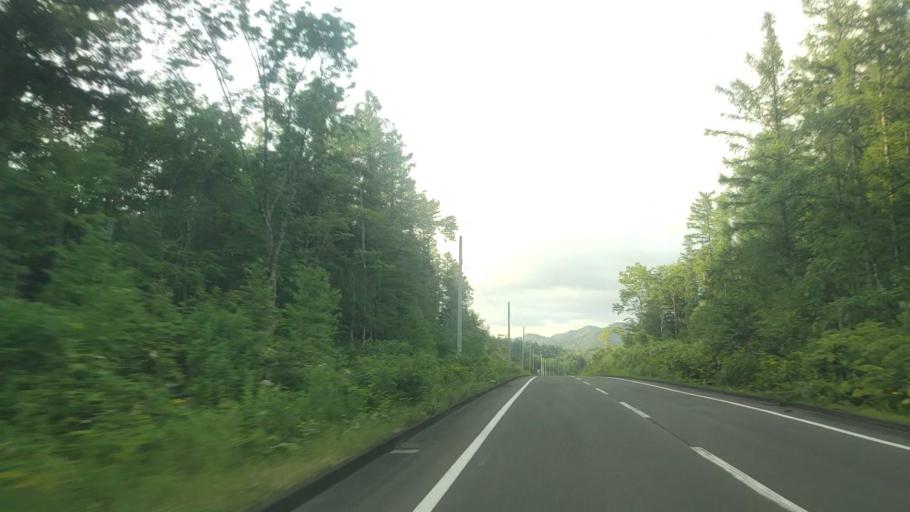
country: JP
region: Hokkaido
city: Bibai
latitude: 43.1046
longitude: 142.0977
